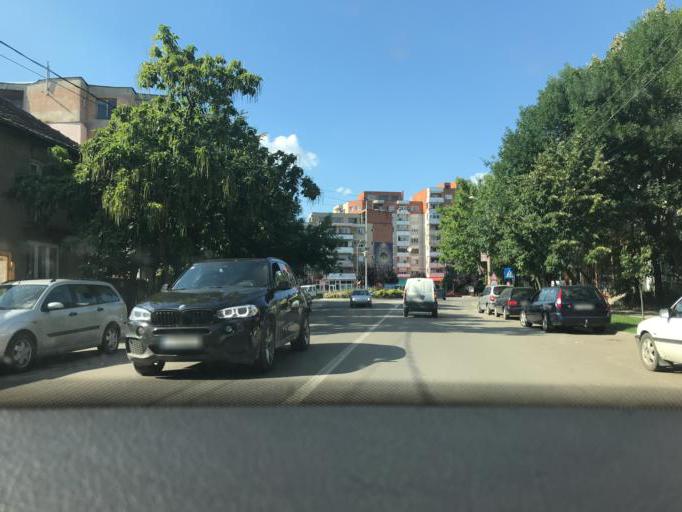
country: RO
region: Bihor
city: Margita
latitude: 47.3425
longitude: 22.3310
